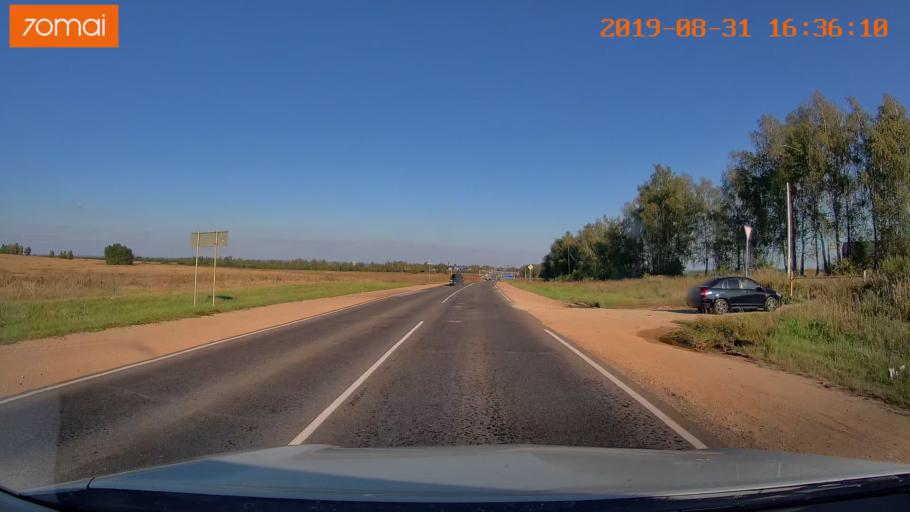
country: RU
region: Kaluga
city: Kurovskoye
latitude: 54.5283
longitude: 35.9671
